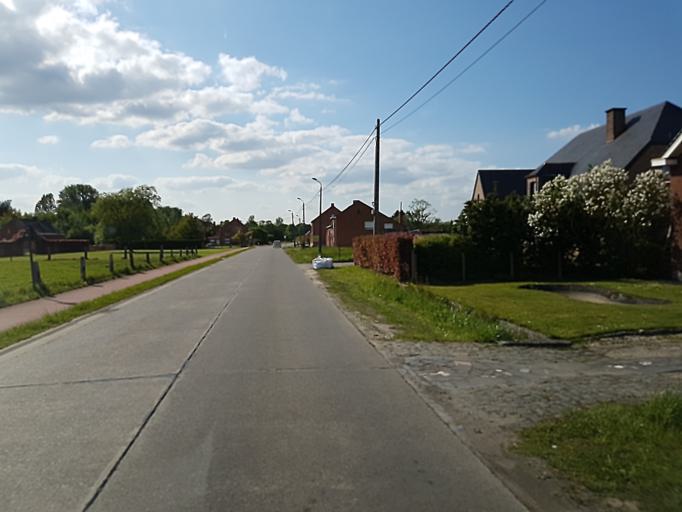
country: BE
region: Flanders
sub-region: Provincie Vlaams-Brabant
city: Begijnendijk
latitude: 51.0254
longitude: 4.7460
